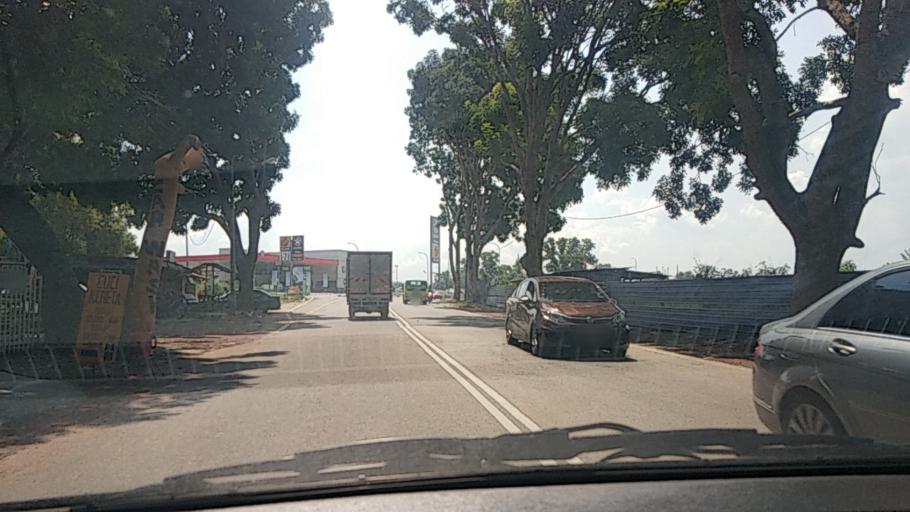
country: MY
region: Kedah
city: Sungai Petani
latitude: 5.6427
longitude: 100.5167
